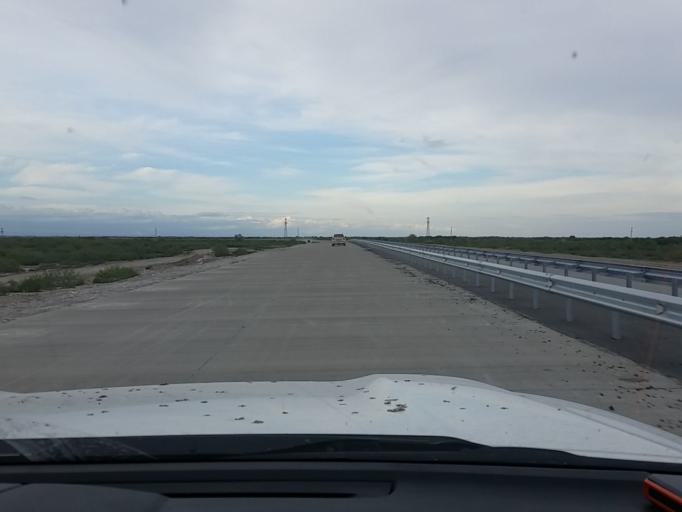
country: KZ
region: Almaty Oblysy
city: Zharkent
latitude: 44.0542
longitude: 80.0085
